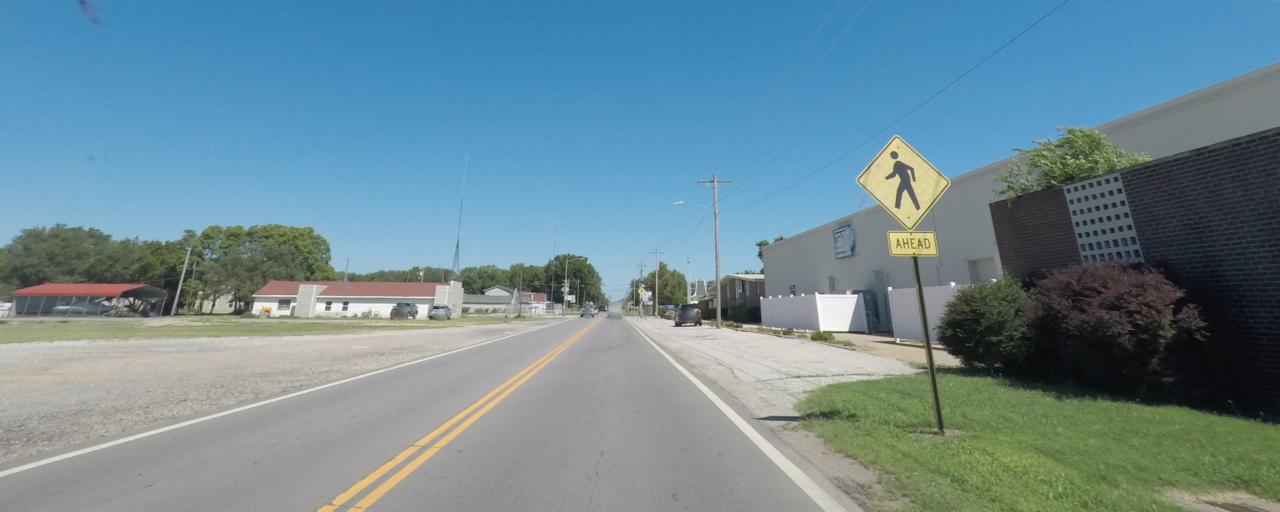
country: US
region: Kansas
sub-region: Sumner County
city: Wellington
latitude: 37.2799
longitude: -97.3942
